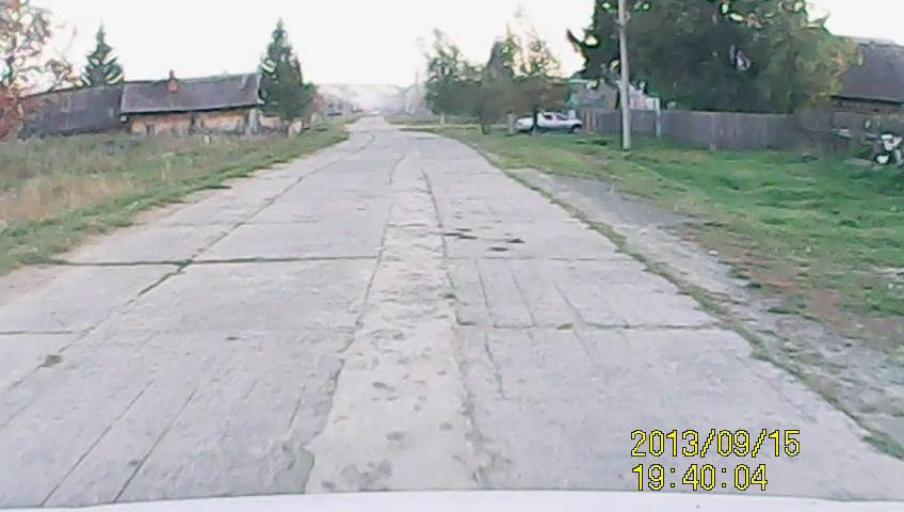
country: RU
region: Chelyabinsk
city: Kyshtym
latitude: 55.8496
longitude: 60.4814
